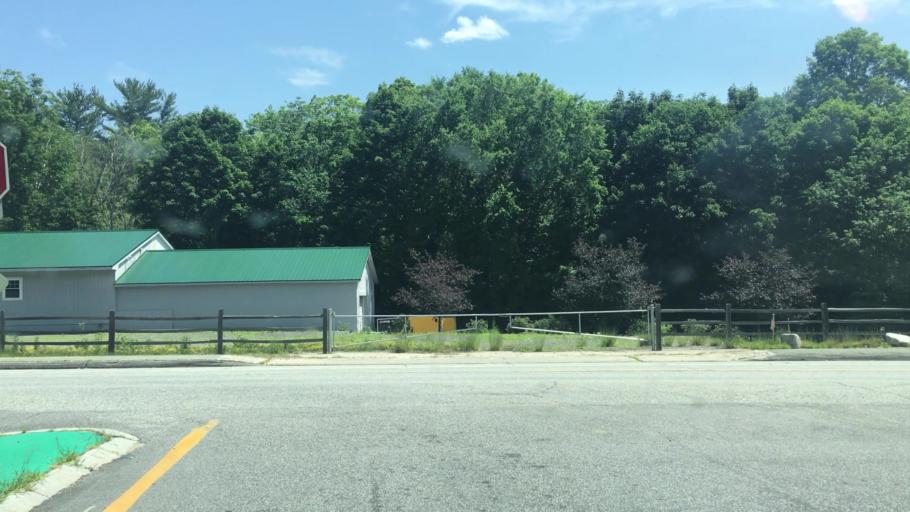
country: US
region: Maine
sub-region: Androscoggin County
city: Livermore
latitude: 44.3842
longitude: -70.2493
